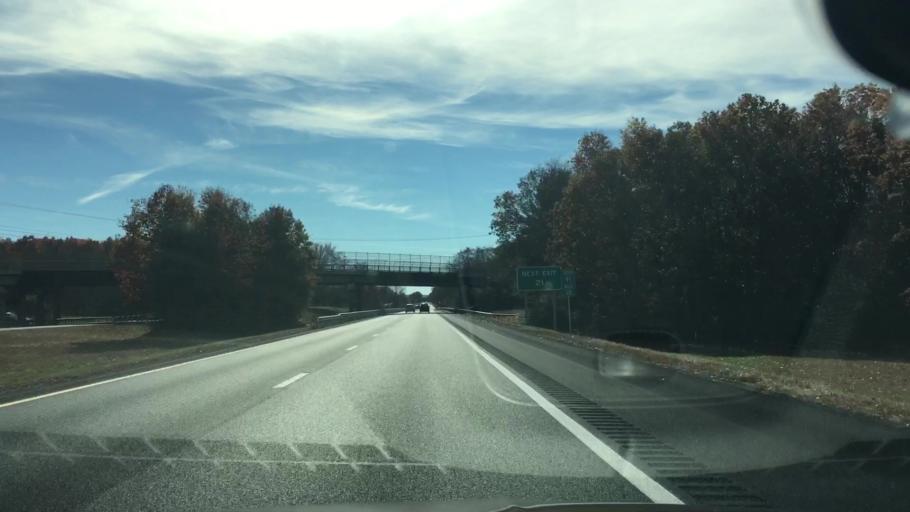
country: US
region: Massachusetts
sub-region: Franklin County
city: Whately
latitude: 42.3997
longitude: -72.6284
